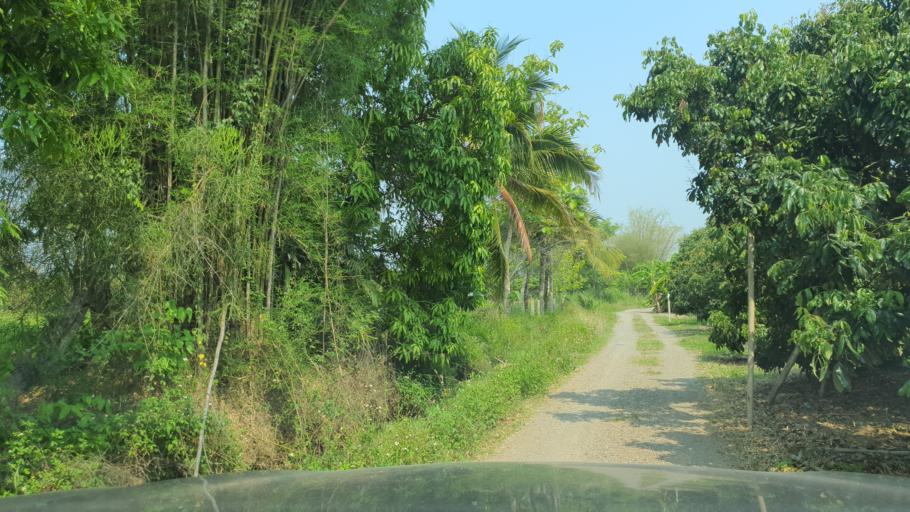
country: TH
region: Chiang Mai
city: Saraphi
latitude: 18.6713
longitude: 98.9967
